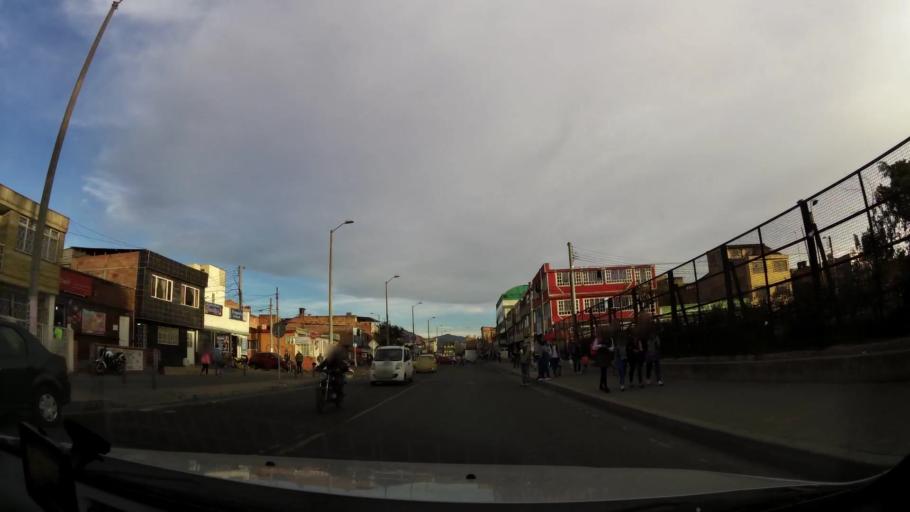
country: CO
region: Cundinamarca
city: Soacha
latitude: 4.6215
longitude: -74.1628
